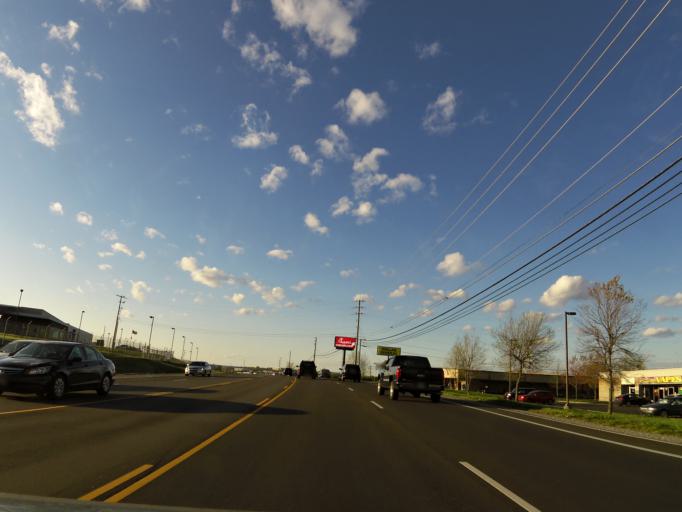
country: US
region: Tennessee
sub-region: Davidson County
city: Goodlettsville
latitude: 36.2752
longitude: -86.6895
